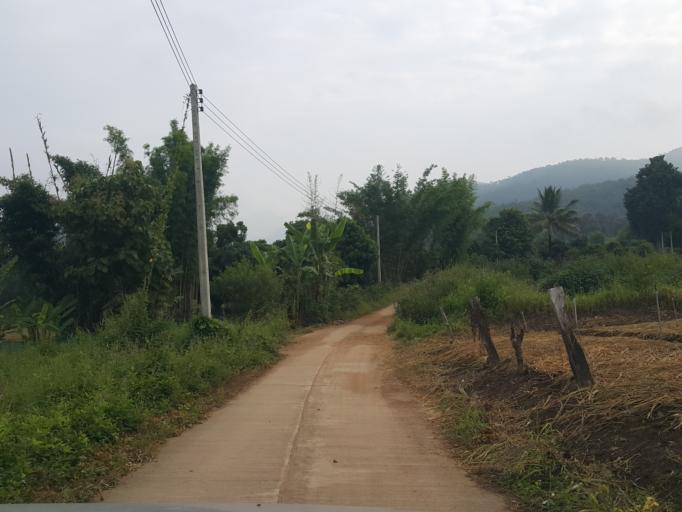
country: TH
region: Mae Hong Son
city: Wiang Nuea
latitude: 19.3796
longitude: 98.4583
